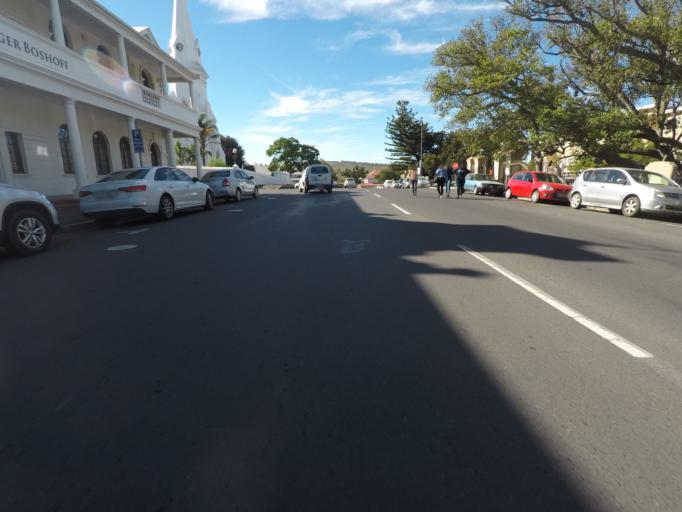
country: ZA
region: Western Cape
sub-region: West Coast District Municipality
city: Malmesbury
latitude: -33.4628
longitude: 18.7302
